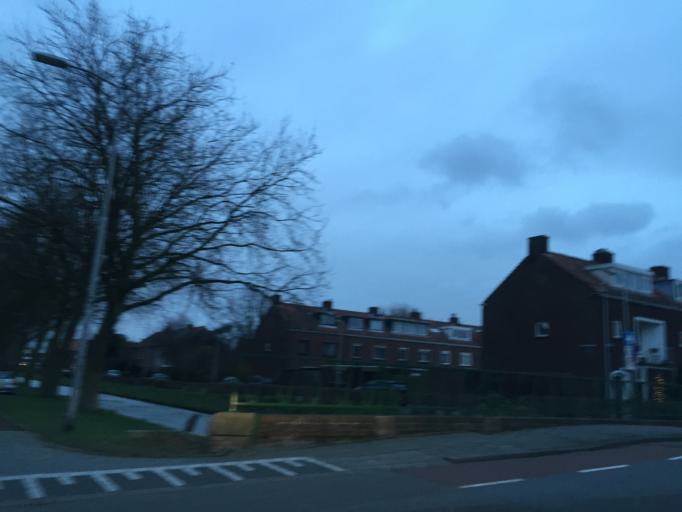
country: NL
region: South Holland
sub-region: Gemeente Pijnacker-Nootdorp
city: Pijnacker
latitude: 52.0218
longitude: 4.4323
